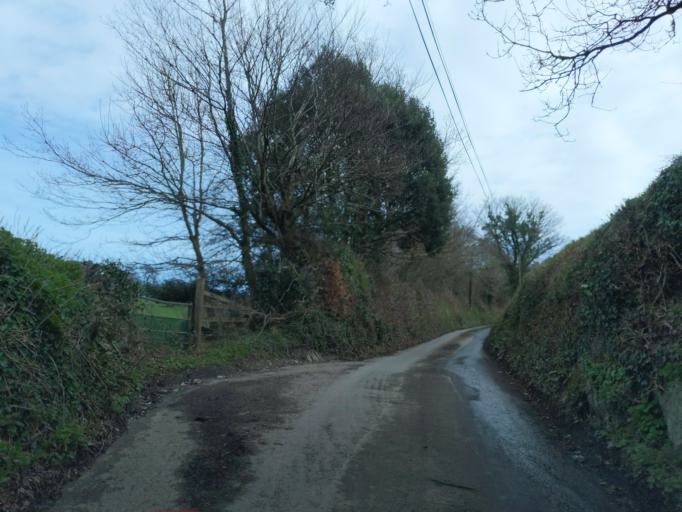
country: GB
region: England
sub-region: Devon
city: Yealmpton
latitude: 50.3636
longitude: -4.0094
